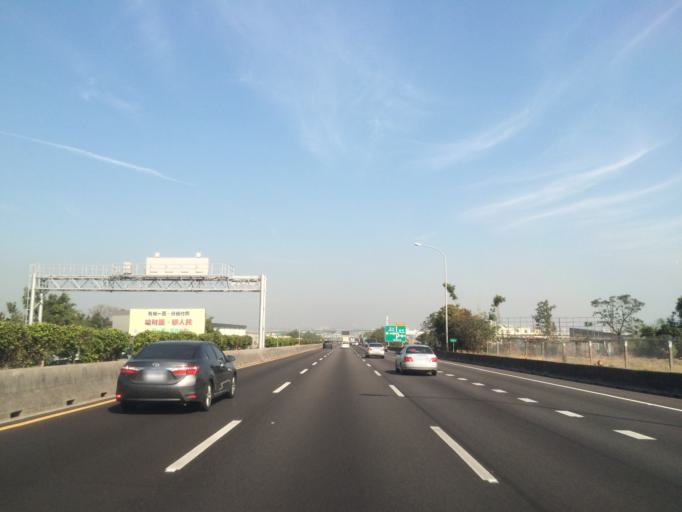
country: TW
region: Taiwan
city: Fengyuan
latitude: 24.2566
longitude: 120.6912
